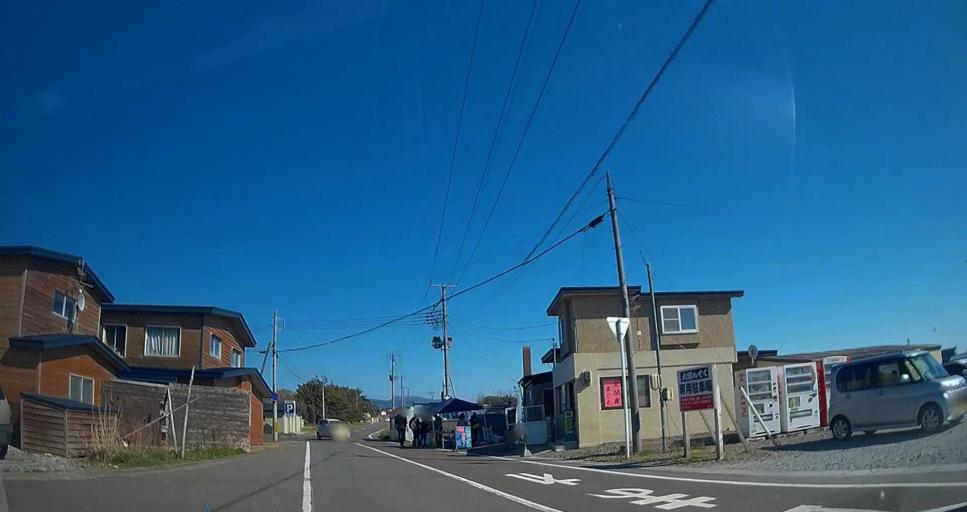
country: JP
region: Hokkaido
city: Hakodate
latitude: 41.5456
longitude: 140.9121
